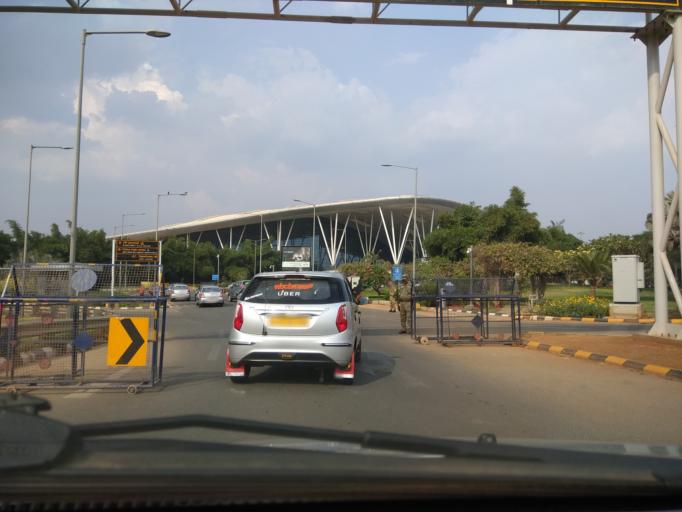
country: IN
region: Karnataka
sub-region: Bangalore Rural
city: Devanhalli
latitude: 13.1991
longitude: 77.7063
